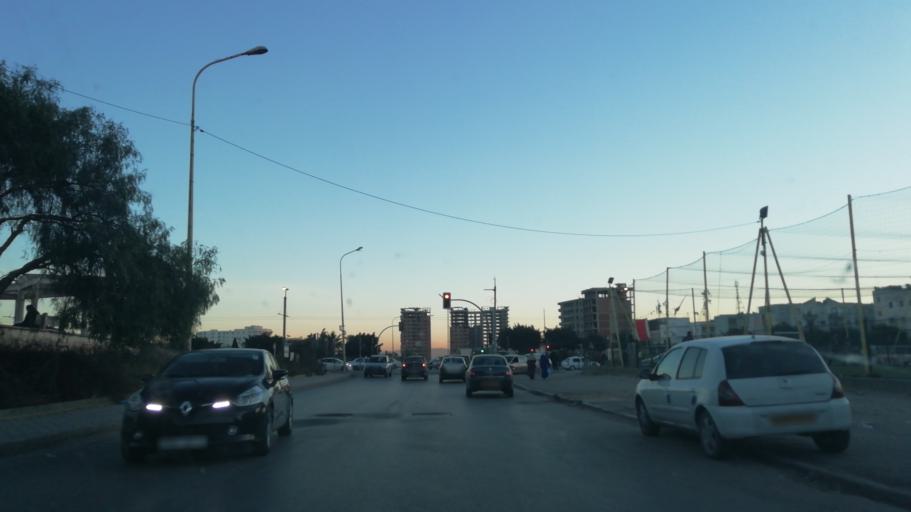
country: DZ
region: Oran
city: Bir el Djir
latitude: 35.7027
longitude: -0.5909
